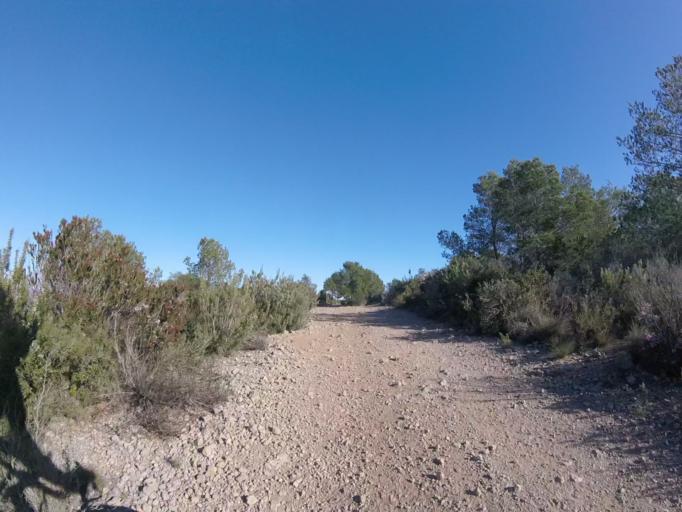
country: ES
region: Valencia
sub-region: Provincia de Castello
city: Orpesa/Oropesa del Mar
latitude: 40.1000
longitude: 0.1115
